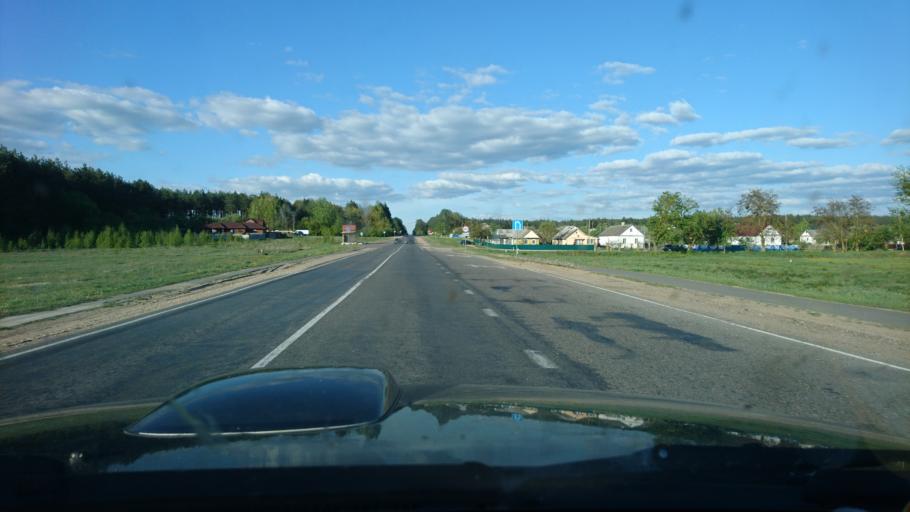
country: BY
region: Brest
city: Ivatsevichy
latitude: 52.7246
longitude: 25.3691
